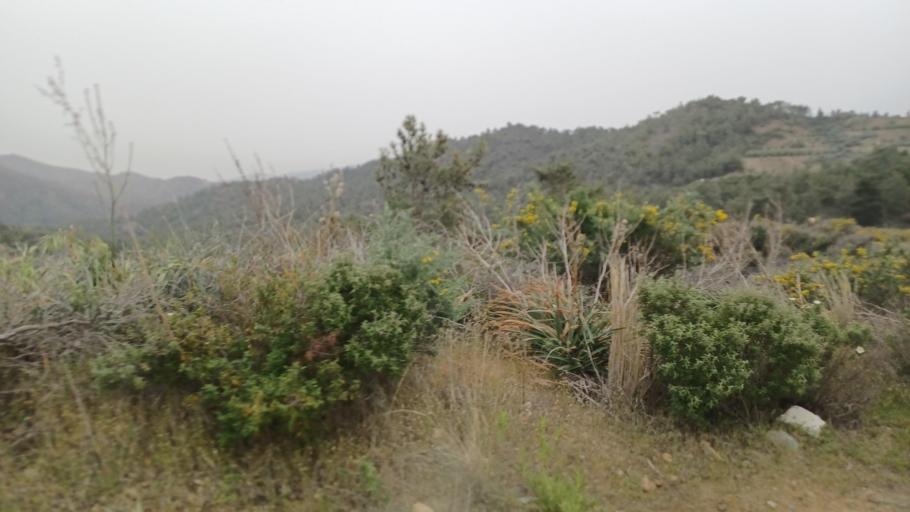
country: CY
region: Limassol
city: Parekklisha
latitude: 34.8624
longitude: 33.0971
